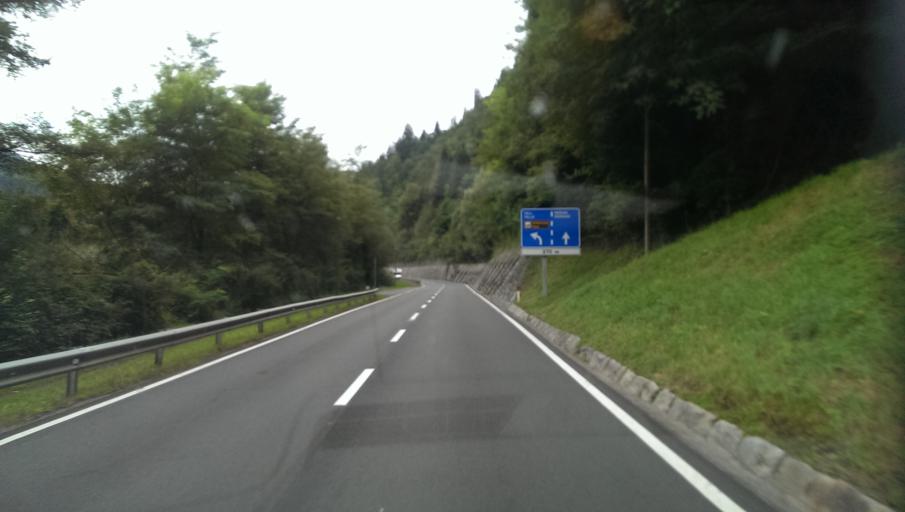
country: IT
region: Trentino-Alto Adige
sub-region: Bolzano
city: Rifiano
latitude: 46.7382
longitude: 11.2005
